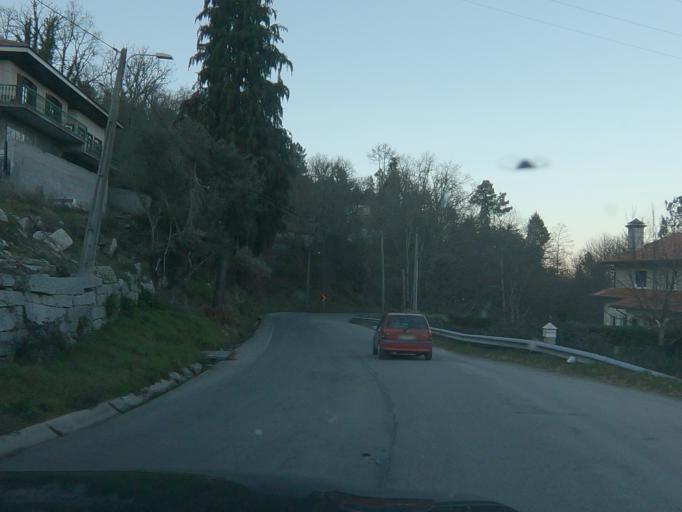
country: PT
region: Vila Real
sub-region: Vila Pouca de Aguiar
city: Vila Pouca de Aguiar
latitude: 41.4959
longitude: -7.6515
